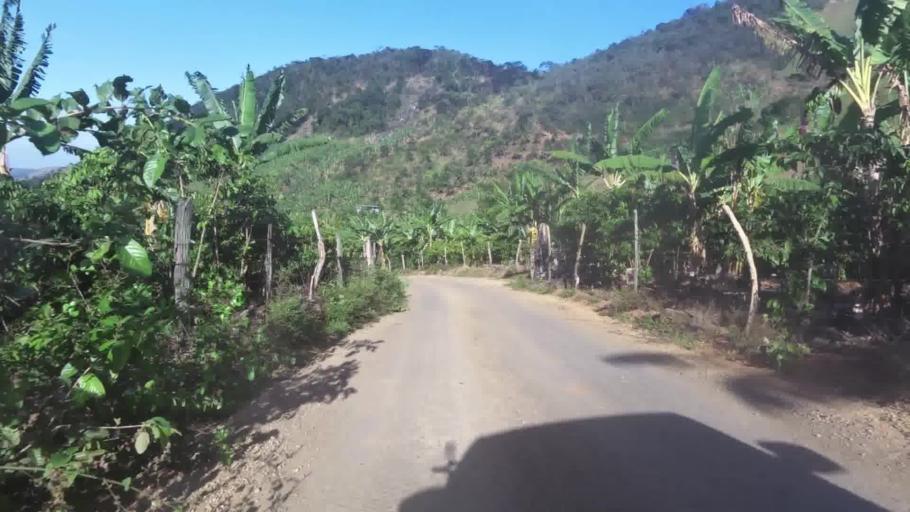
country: BR
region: Espirito Santo
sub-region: Iconha
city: Iconha
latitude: -20.7504
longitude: -40.8031
